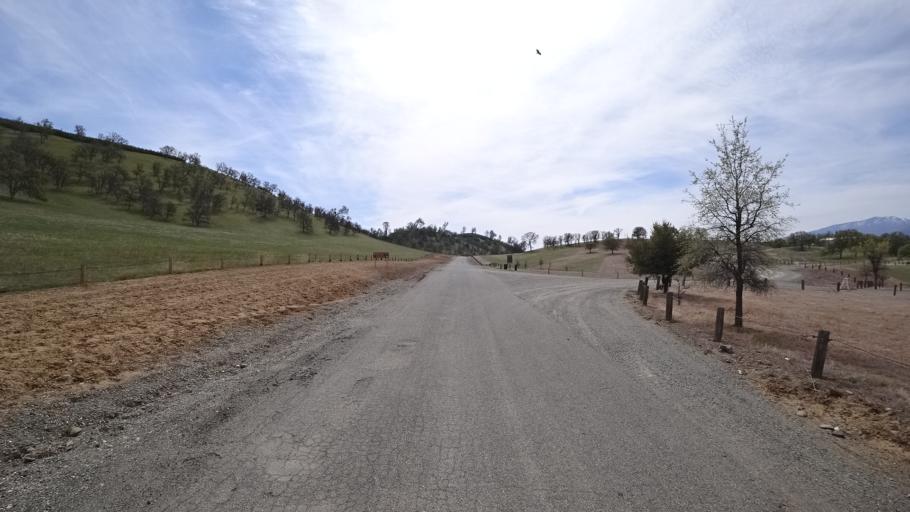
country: US
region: California
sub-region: Glenn County
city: Willows
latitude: 39.5928
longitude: -122.5241
